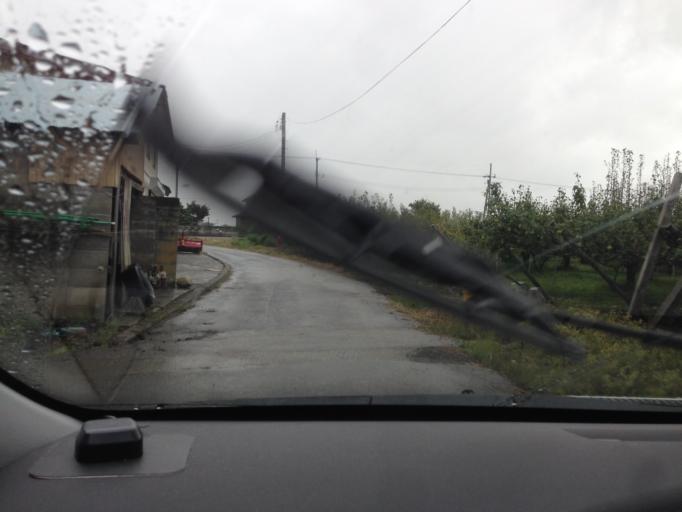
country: JP
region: Fukushima
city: Kitakata
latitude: 37.4628
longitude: 139.8732
